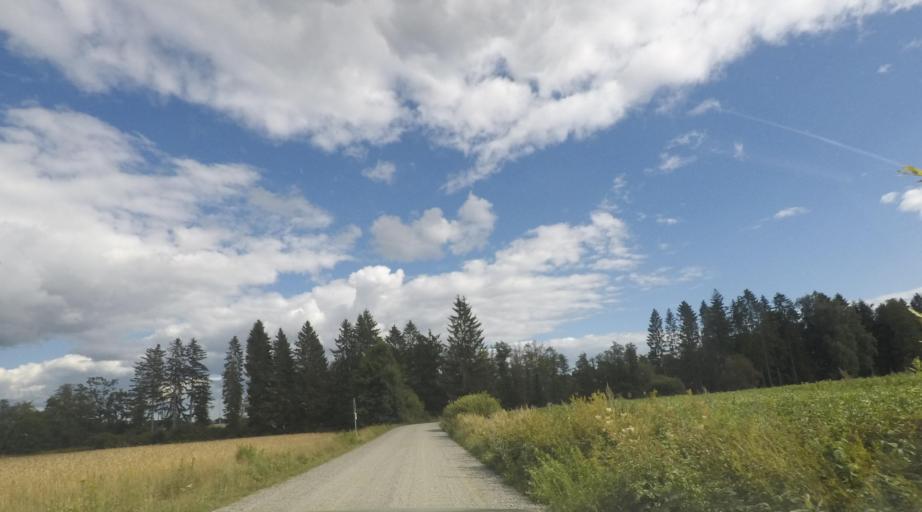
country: SE
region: Stockholm
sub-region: Sodertalje Kommun
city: Pershagen
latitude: 59.1067
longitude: 17.6775
